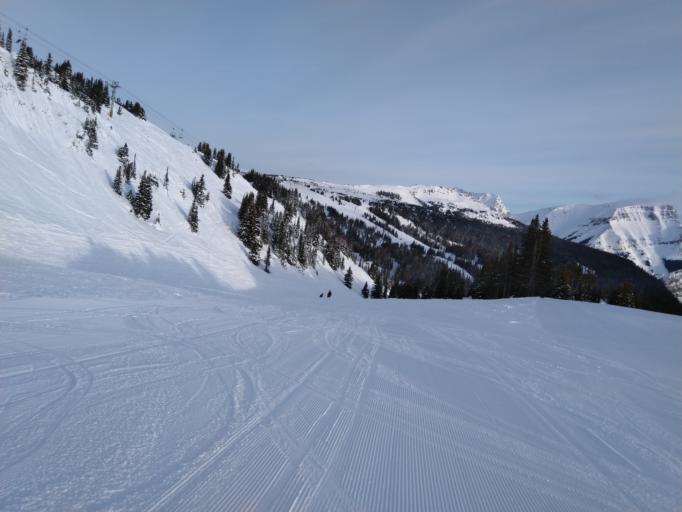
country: CA
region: Alberta
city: Banff
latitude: 51.0725
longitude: -115.7830
